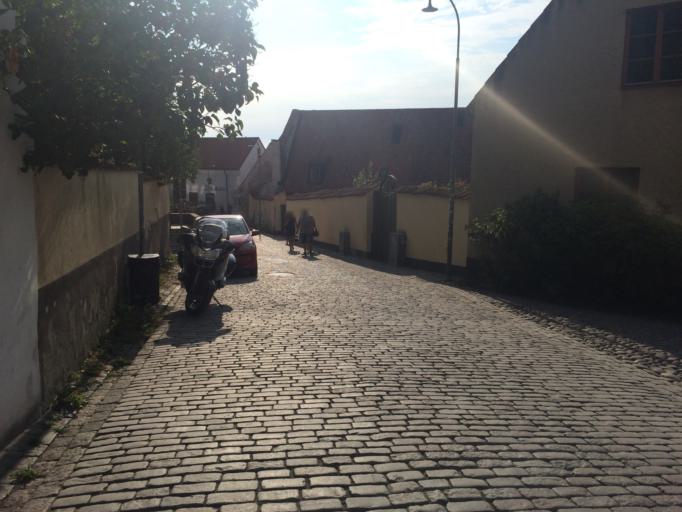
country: SE
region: Gotland
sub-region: Gotland
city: Visby
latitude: 57.6386
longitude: 18.2949
